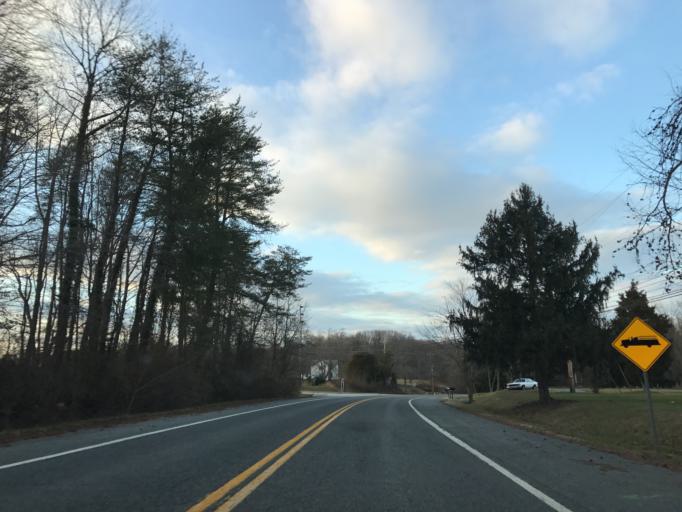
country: US
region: Maryland
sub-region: Cecil County
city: Charlestown
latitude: 39.5181
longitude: -75.9538
